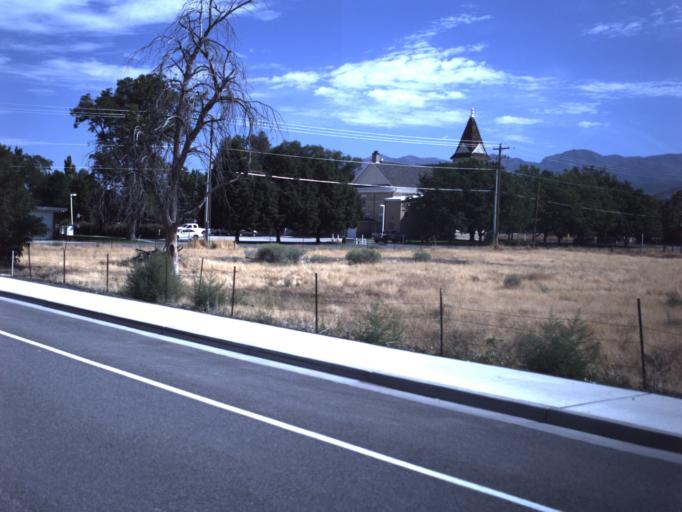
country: US
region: Utah
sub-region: Juab County
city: Nephi
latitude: 39.5567
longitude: -111.8638
